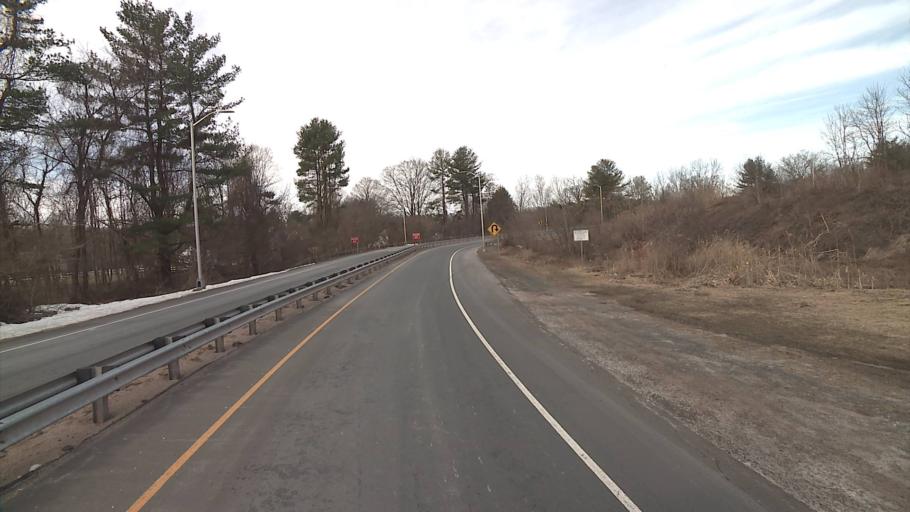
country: US
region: Connecticut
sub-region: Hartford County
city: Windsor Locks
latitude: 41.9169
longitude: -72.6863
